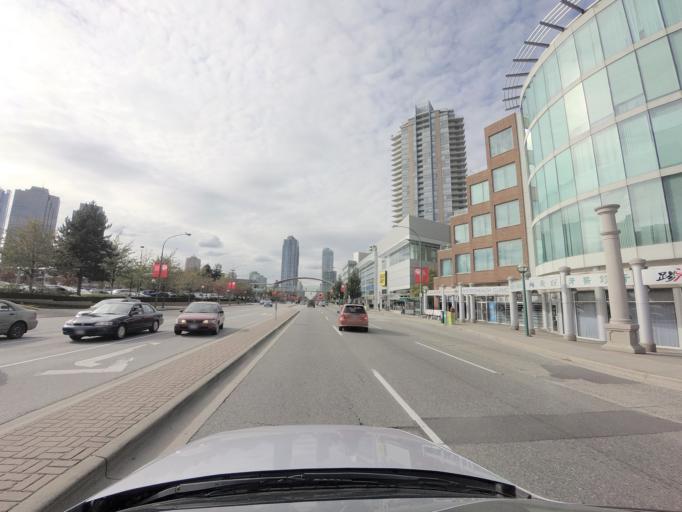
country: CA
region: British Columbia
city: Burnaby
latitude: 49.2270
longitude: -122.9947
